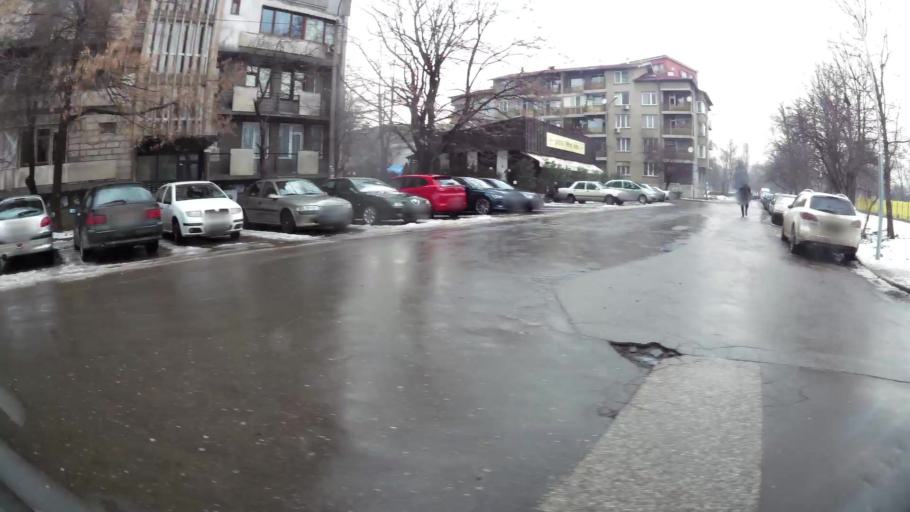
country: BG
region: Sofia-Capital
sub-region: Stolichna Obshtina
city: Sofia
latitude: 42.6802
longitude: 23.2965
